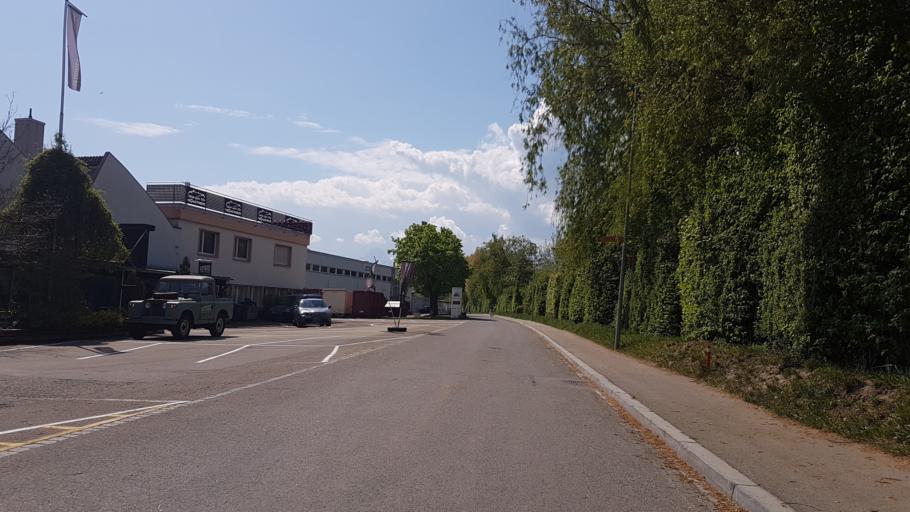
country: CH
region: Bern
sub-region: Bern-Mittelland District
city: Toffen
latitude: 46.8625
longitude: 7.4960
